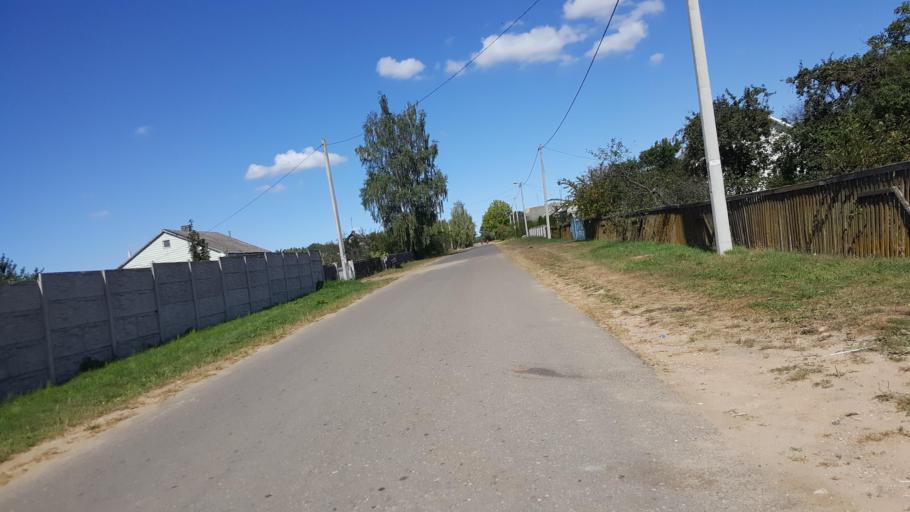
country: BY
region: Brest
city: Vysokaye
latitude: 52.2602
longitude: 23.4294
